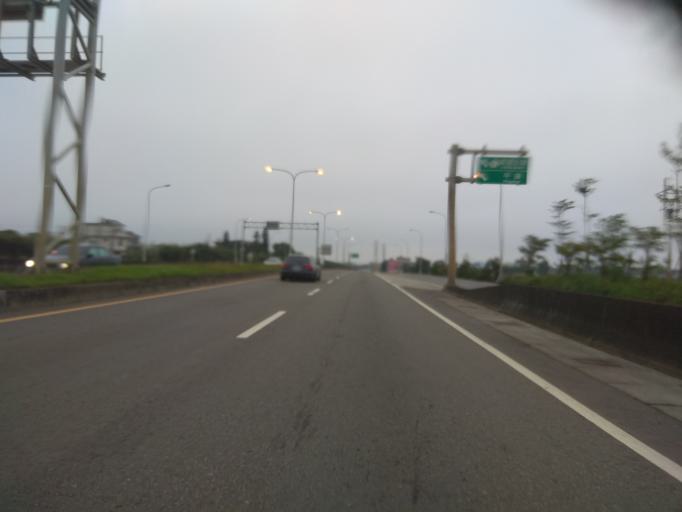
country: TW
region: Taiwan
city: Taoyuan City
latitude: 24.9874
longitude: 121.1235
